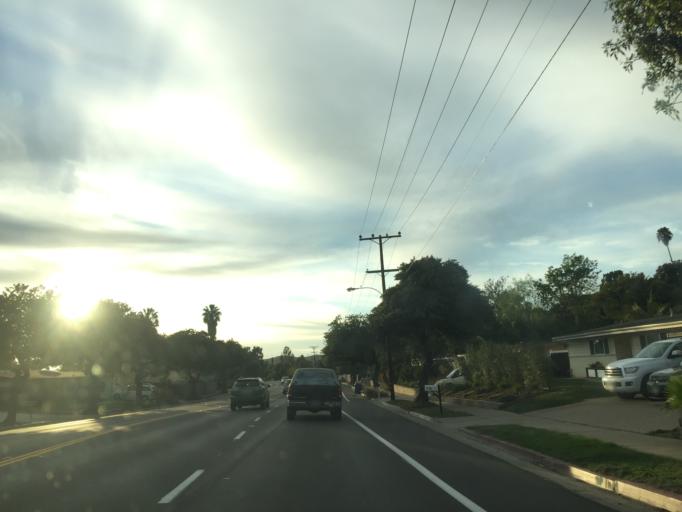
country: US
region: California
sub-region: Santa Barbara County
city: Goleta
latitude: 34.4514
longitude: -119.8209
